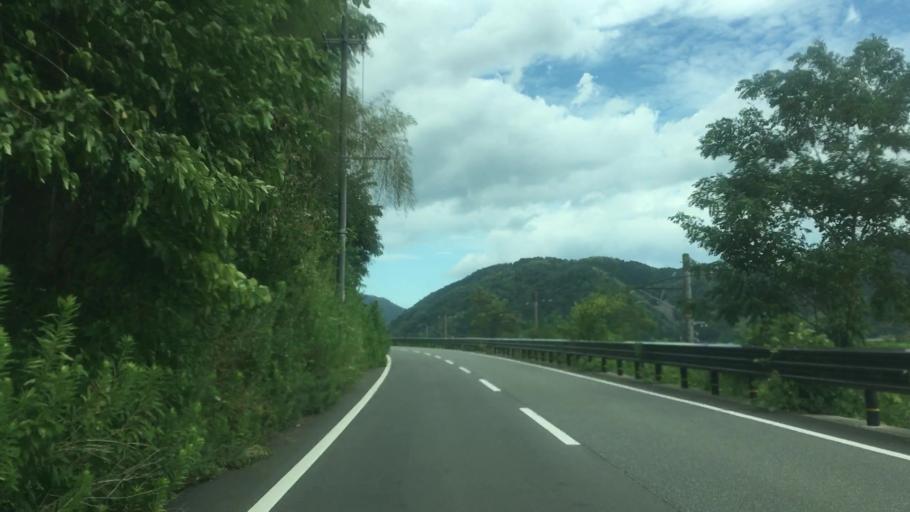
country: JP
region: Hyogo
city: Toyooka
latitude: 35.5734
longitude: 134.8050
